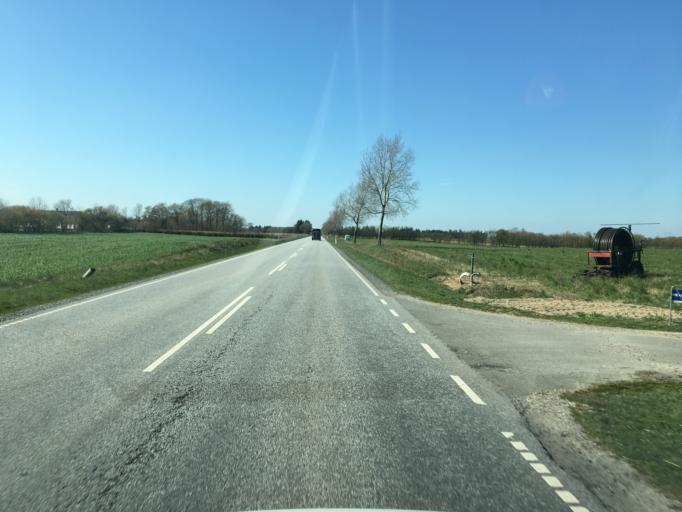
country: DK
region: South Denmark
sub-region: Aabenraa Kommune
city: Krusa
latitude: 54.9434
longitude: 9.3577
